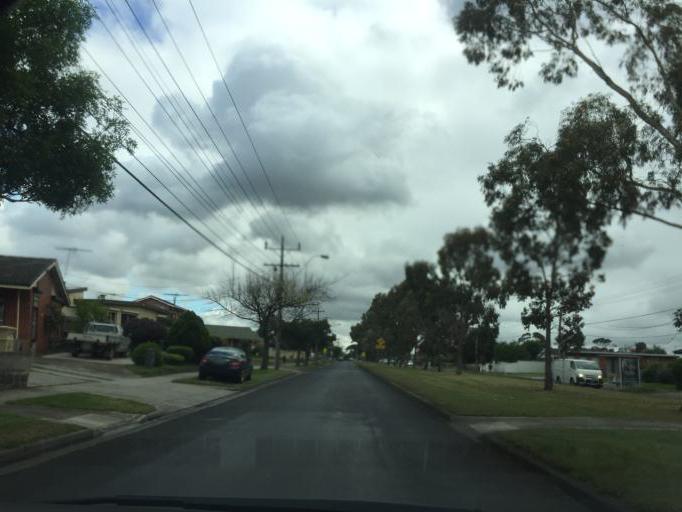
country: AU
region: Victoria
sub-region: Brimbank
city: Sunshine West
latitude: -37.8020
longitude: 144.8186
